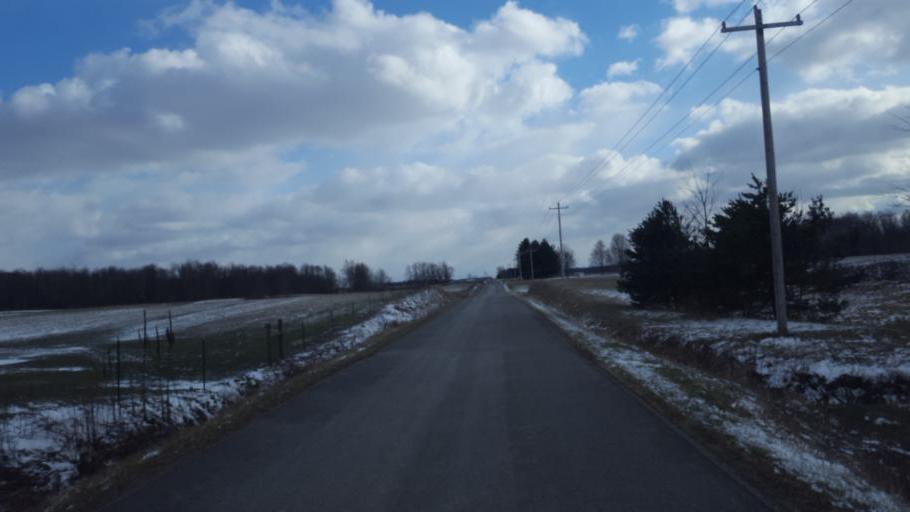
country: US
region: Ohio
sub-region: Crawford County
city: Galion
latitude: 40.6942
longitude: -82.7178
